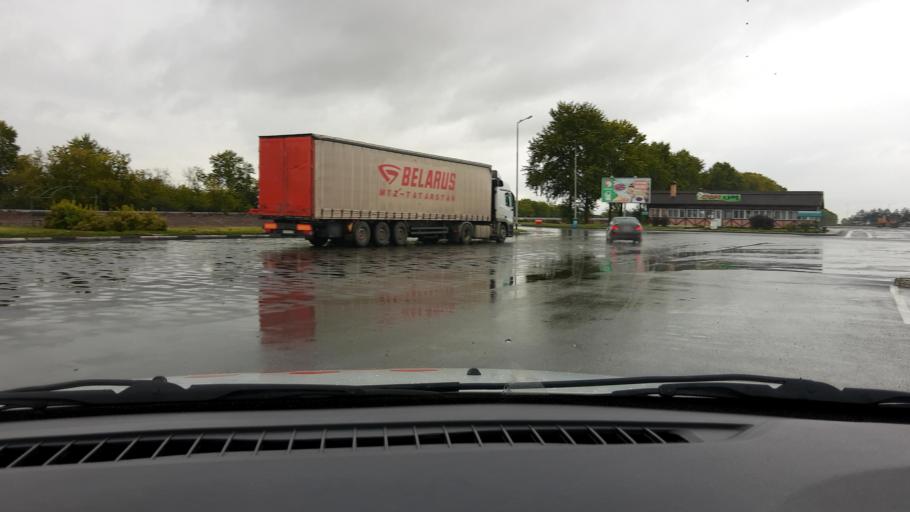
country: RU
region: Chuvashia
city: Yantikovo
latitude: 55.8054
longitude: 47.9210
